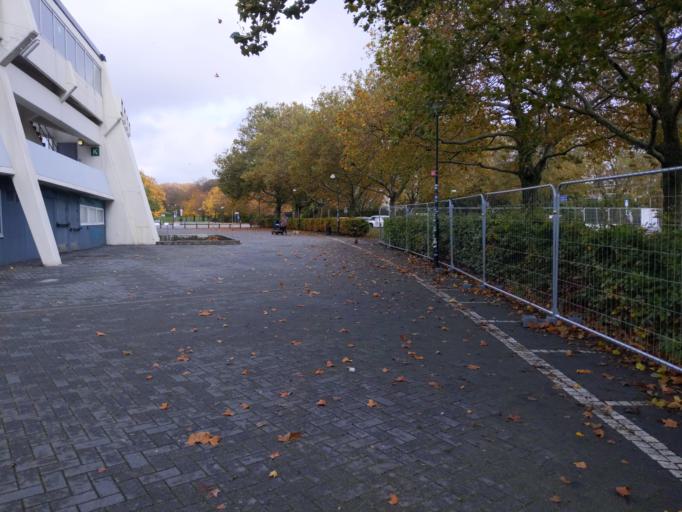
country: SE
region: Skane
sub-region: Malmo
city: Malmoe
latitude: 55.5853
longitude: 12.9904
